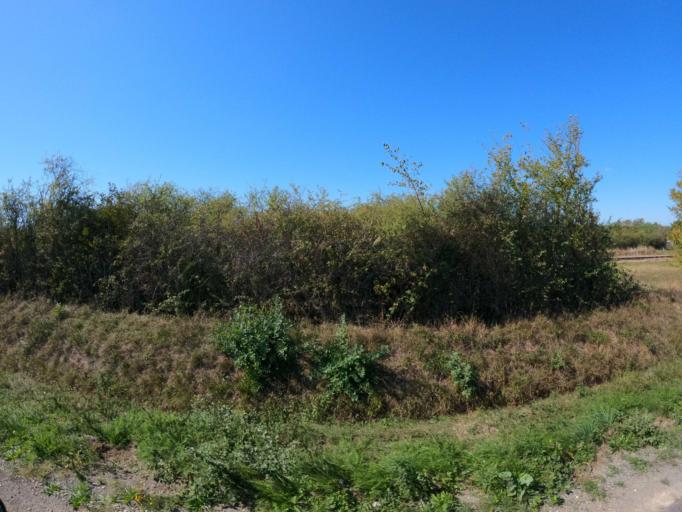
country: FR
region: Poitou-Charentes
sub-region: Departement de la Vienne
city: Lathus-Saint-Remy
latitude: 46.3629
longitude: 0.9407
